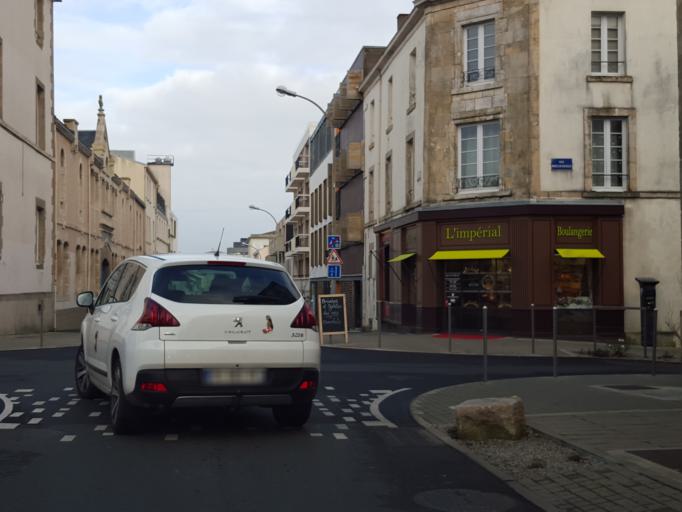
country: FR
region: Pays de la Loire
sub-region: Departement de la Vendee
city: La Roche-sur-Yon
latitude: 46.6713
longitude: -1.4258
